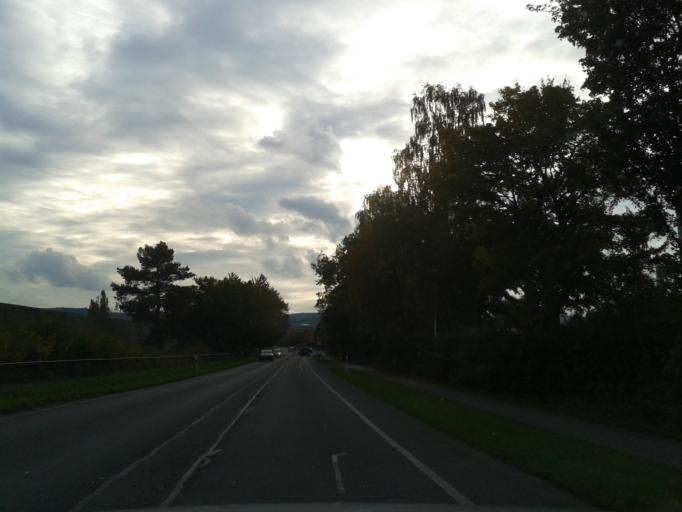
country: DE
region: North Rhine-Westphalia
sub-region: Regierungsbezirk Detmold
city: Horn-Bad Meinberg
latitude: 51.8846
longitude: 8.9617
